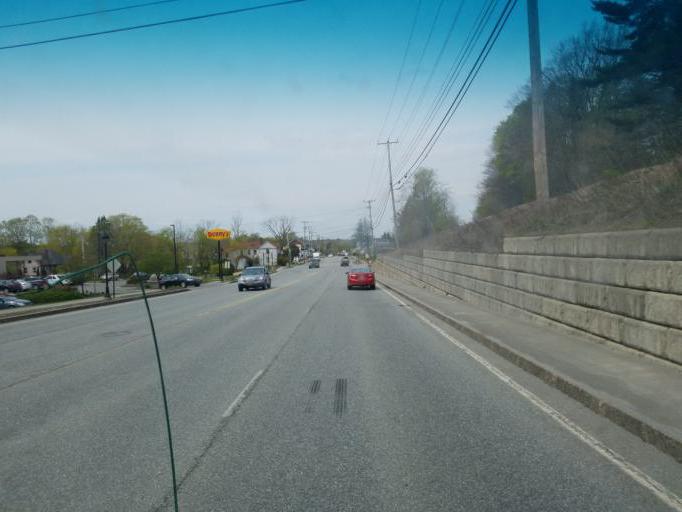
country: US
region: Maine
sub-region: Hancock County
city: Ellsworth
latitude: 44.5395
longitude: -68.4160
